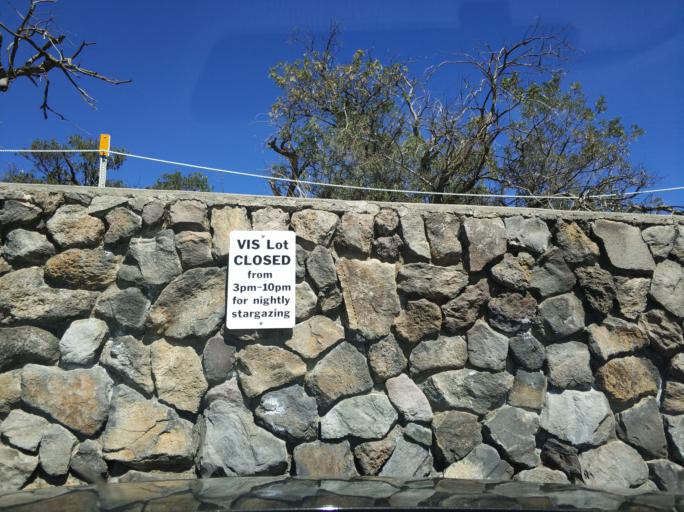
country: US
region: Hawaii
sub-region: Hawaii County
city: Honoka'a
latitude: 19.7594
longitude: -155.4560
